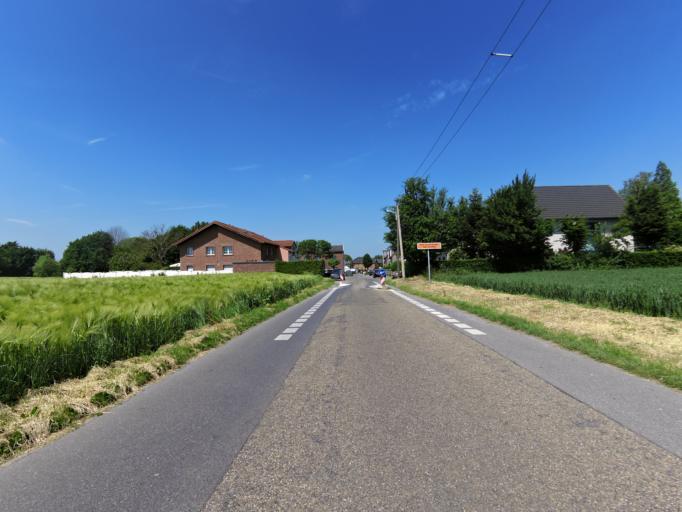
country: DE
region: North Rhine-Westphalia
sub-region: Regierungsbezirk Koln
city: Herzogenrath
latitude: 50.8959
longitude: 6.0936
